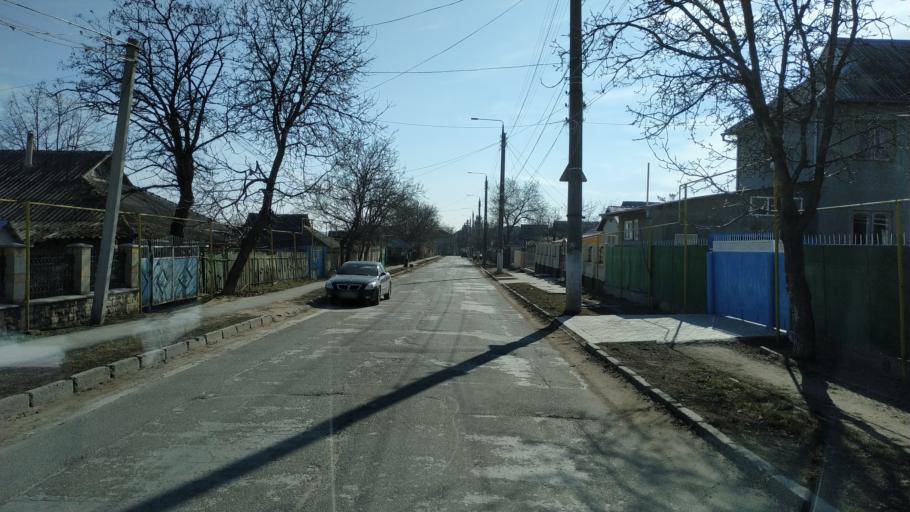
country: MD
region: Nisporeni
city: Nisporeni
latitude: 47.0815
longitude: 28.1675
